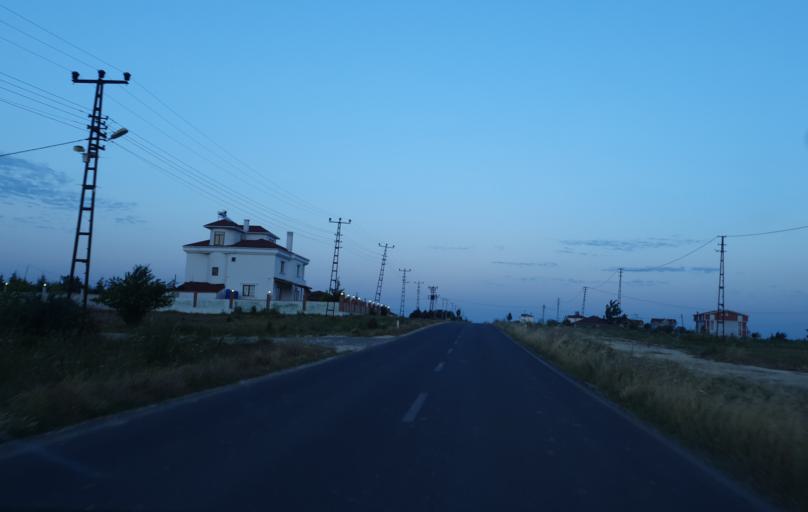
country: TR
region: Tekirdag
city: Velimese
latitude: 41.3443
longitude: 27.8959
